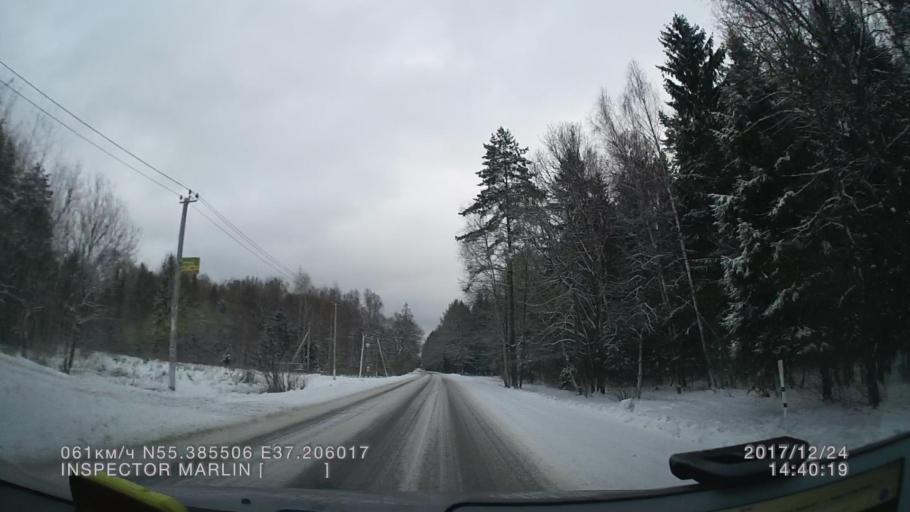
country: RU
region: Moskovskaya
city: Troitsk
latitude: 55.3854
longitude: 37.2063
